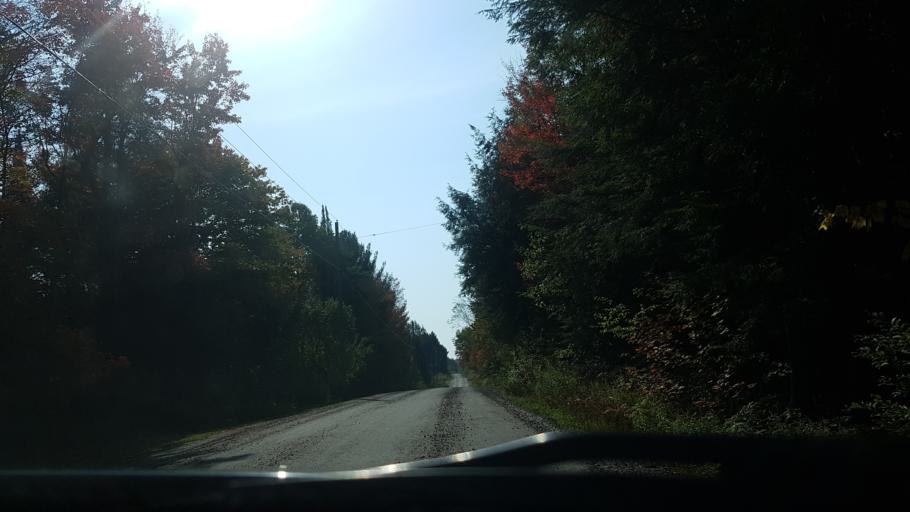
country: CA
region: Ontario
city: Bracebridge
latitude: 44.9302
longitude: -79.2349
